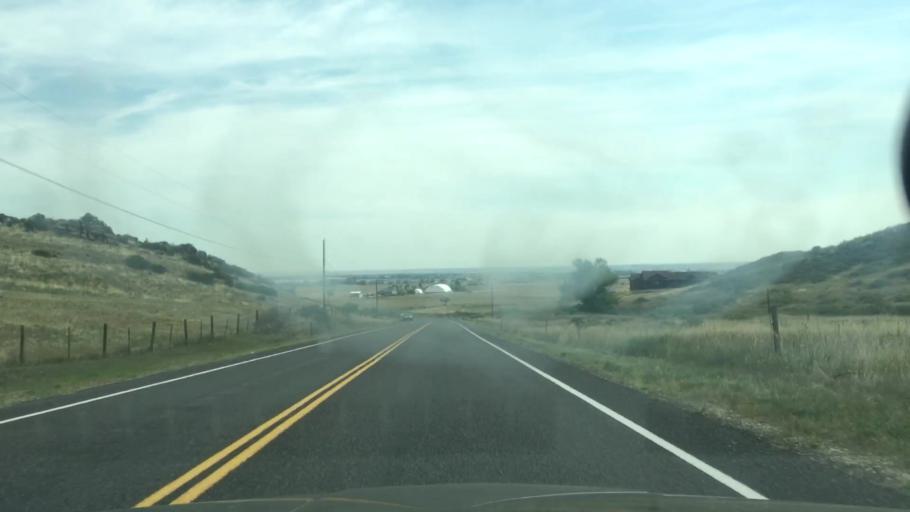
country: US
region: Colorado
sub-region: Larimer County
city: Campion
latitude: 40.3380
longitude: -105.1804
